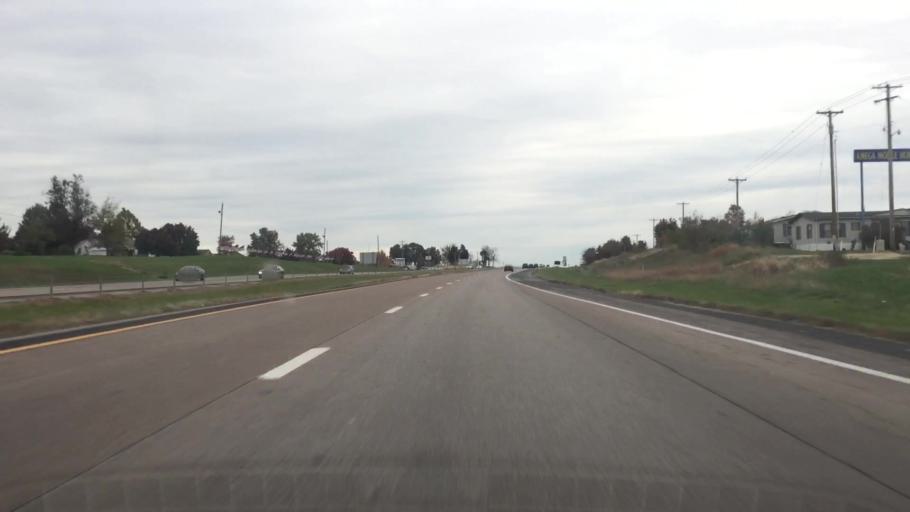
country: US
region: Missouri
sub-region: Boone County
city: Ashland
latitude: 38.7785
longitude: -92.2523
